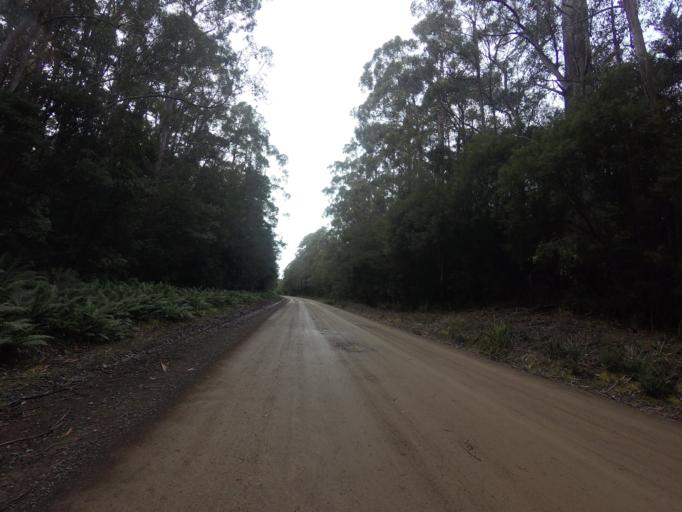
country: AU
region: Tasmania
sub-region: Huon Valley
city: Geeveston
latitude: -43.5076
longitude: 146.8766
